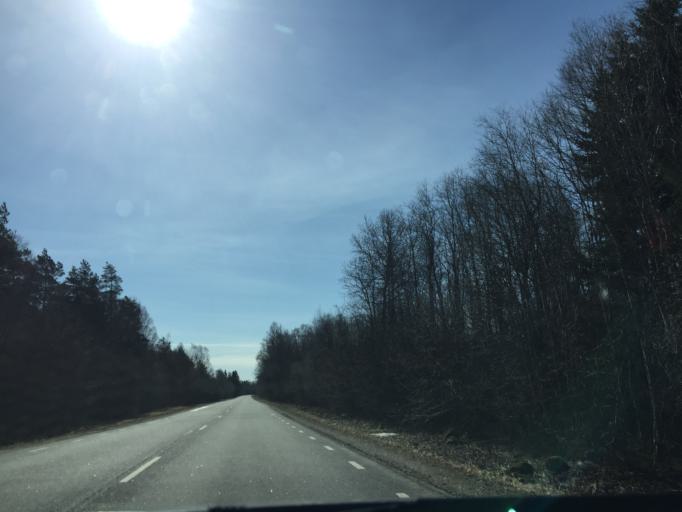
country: EE
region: Laeaene
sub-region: Lihula vald
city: Lihula
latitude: 58.6026
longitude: 23.6988
